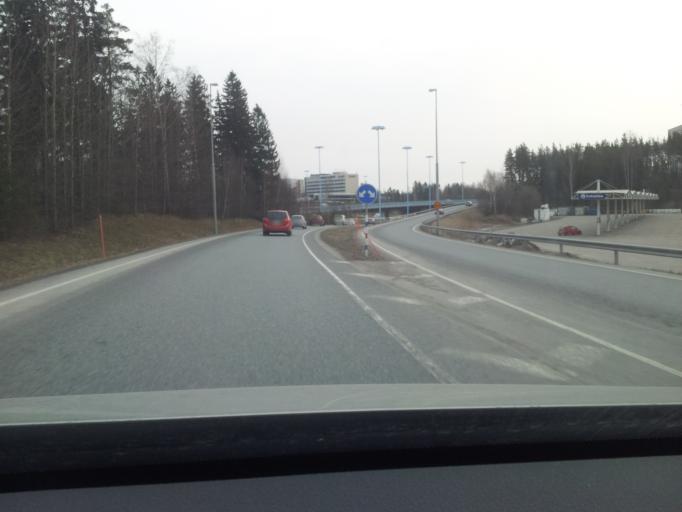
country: FI
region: Uusimaa
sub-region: Helsinki
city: Kauniainen
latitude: 60.2038
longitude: 24.7499
